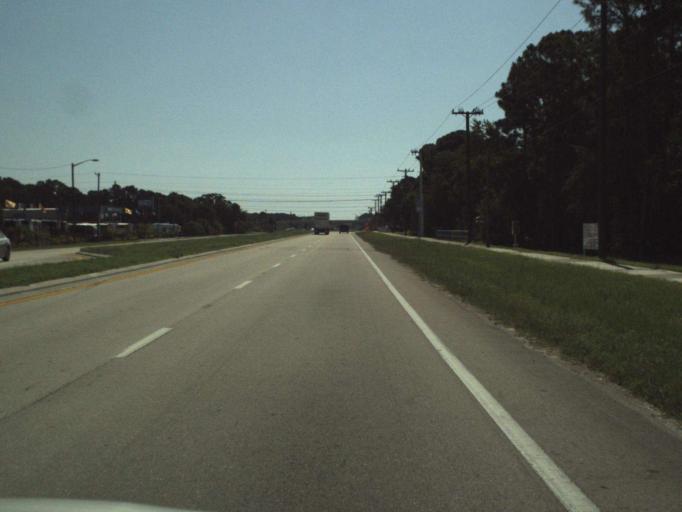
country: US
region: Florida
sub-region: Brevard County
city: Cocoa West
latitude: 28.3597
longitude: -80.8016
